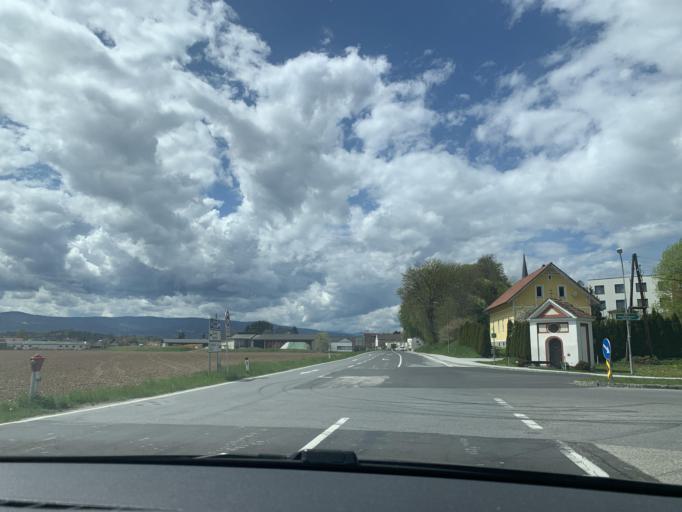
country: AT
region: Styria
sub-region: Politischer Bezirk Graz-Umgebung
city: Unterpremstatten
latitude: 46.9456
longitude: 15.3824
